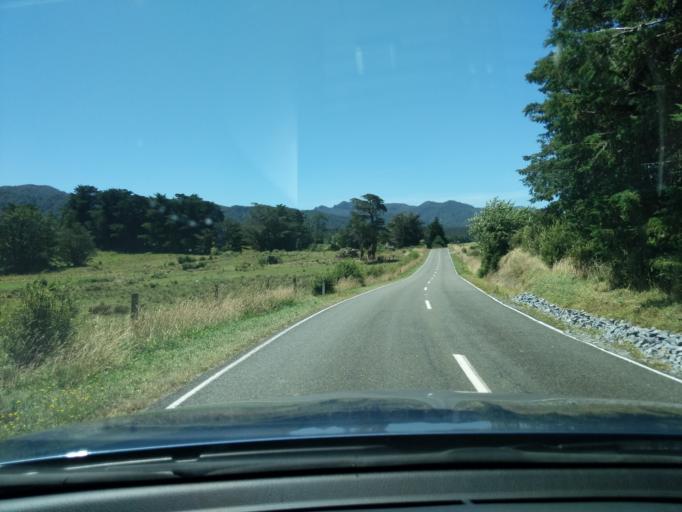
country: NZ
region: Tasman
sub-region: Tasman District
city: Takaka
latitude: -40.7559
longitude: 172.5613
